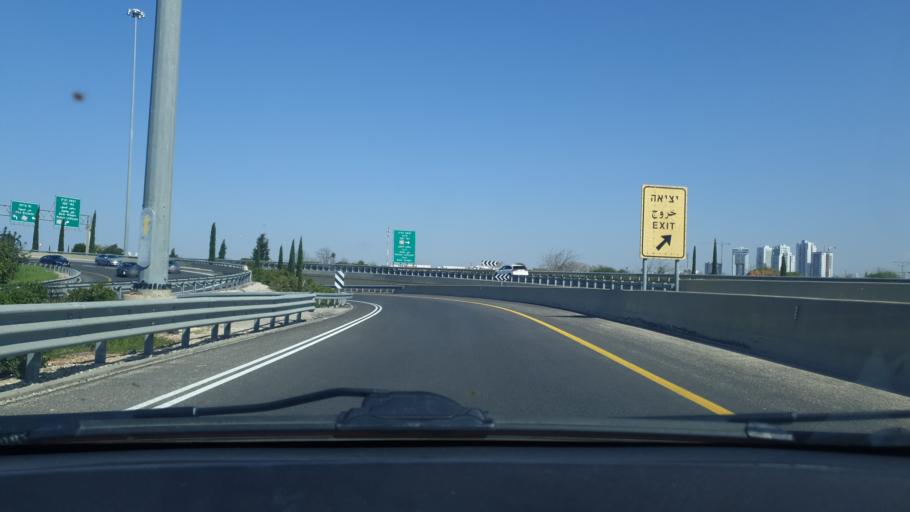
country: IL
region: Central District
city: Ness Ziona
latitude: 31.9384
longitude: 34.8175
